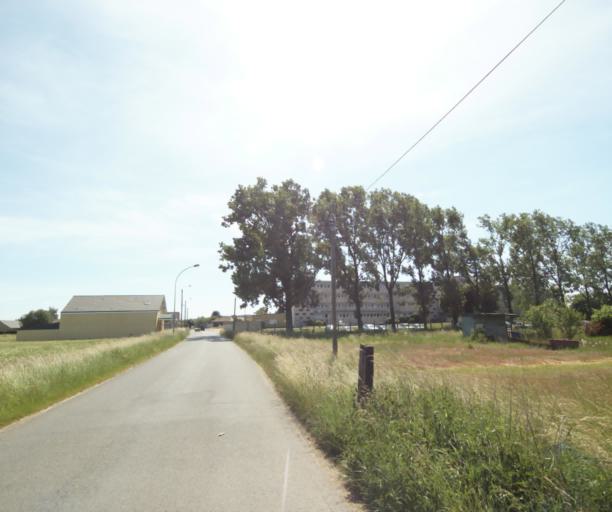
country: FR
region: Champagne-Ardenne
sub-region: Departement des Ardennes
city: Warcq
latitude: 49.7692
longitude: 4.6869
